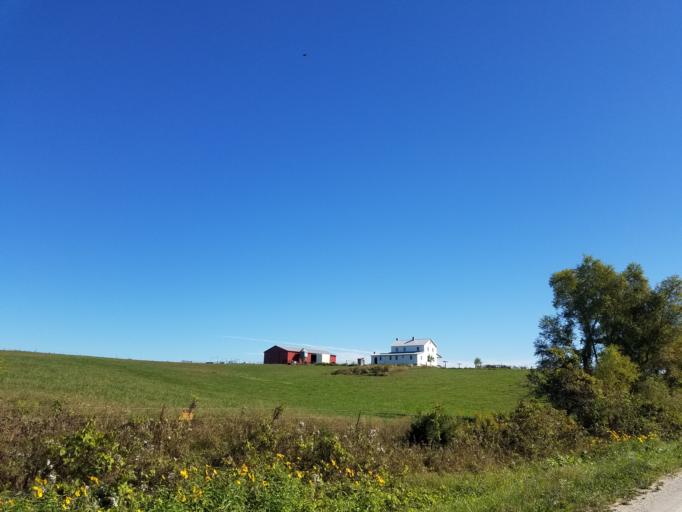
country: US
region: Iowa
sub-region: Decatur County
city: Lamoni
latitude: 40.6093
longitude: -93.8540
